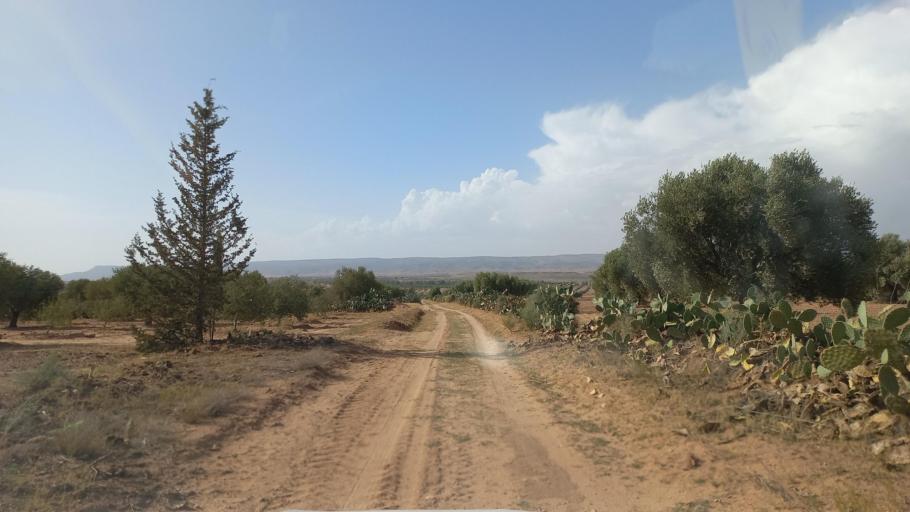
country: TN
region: Al Qasrayn
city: Kasserine
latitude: 35.2109
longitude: 8.9542
